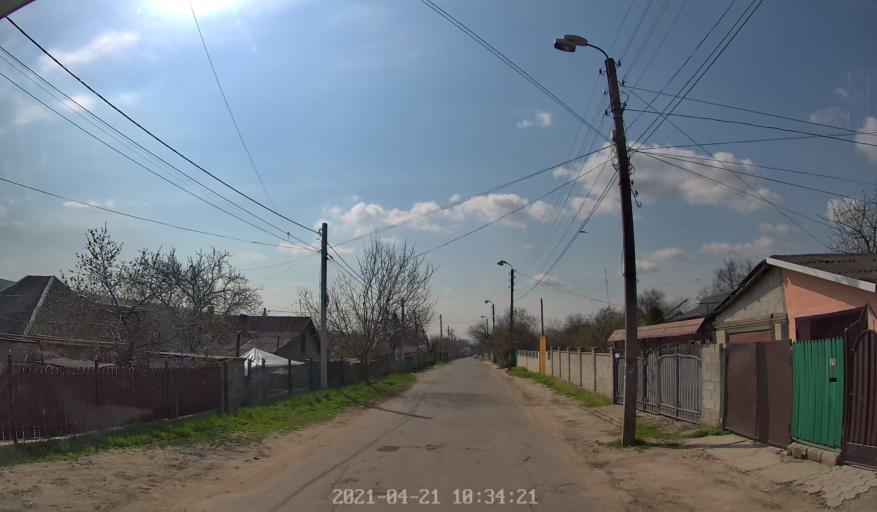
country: MD
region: Chisinau
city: Singera
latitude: 46.9829
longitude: 28.9368
